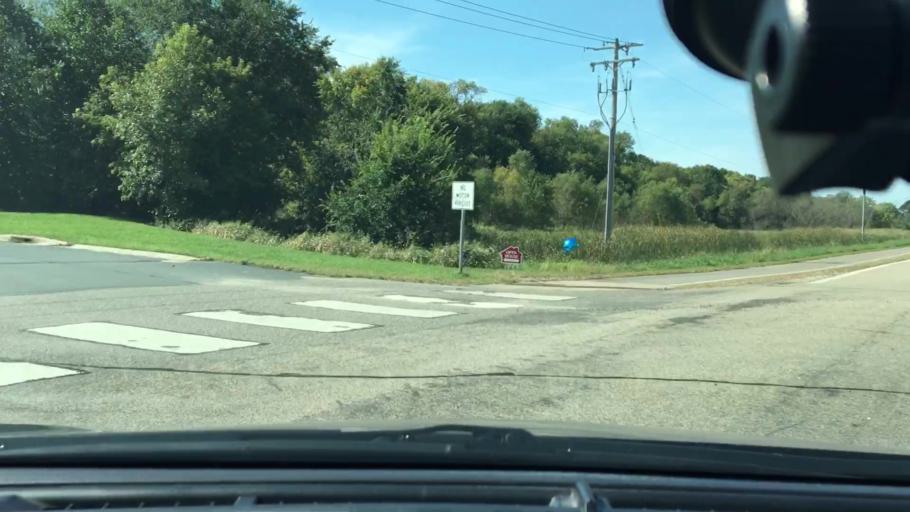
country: US
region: Minnesota
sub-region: Wright County
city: Hanover
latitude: 45.1649
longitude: -93.6774
